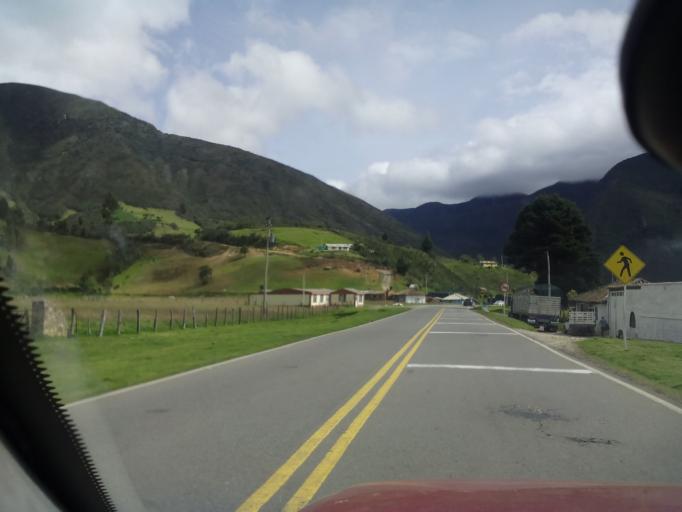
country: CO
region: Boyaca
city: Arcabuco
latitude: 5.7048
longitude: -73.3720
